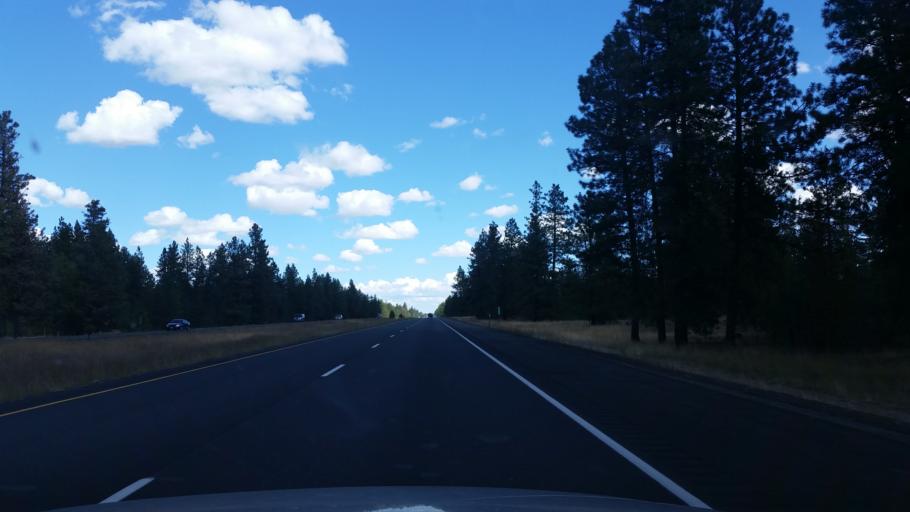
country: US
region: Washington
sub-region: Spokane County
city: Medical Lake
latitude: 47.4796
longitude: -117.7269
